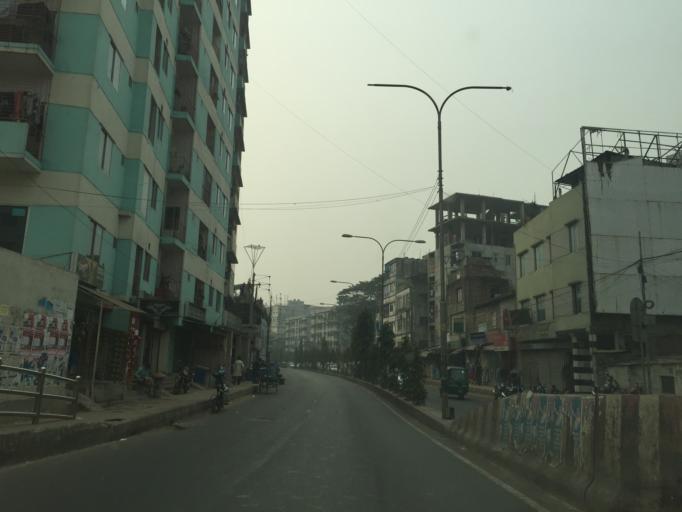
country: BD
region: Dhaka
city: Paltan
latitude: 23.7642
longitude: 90.3930
